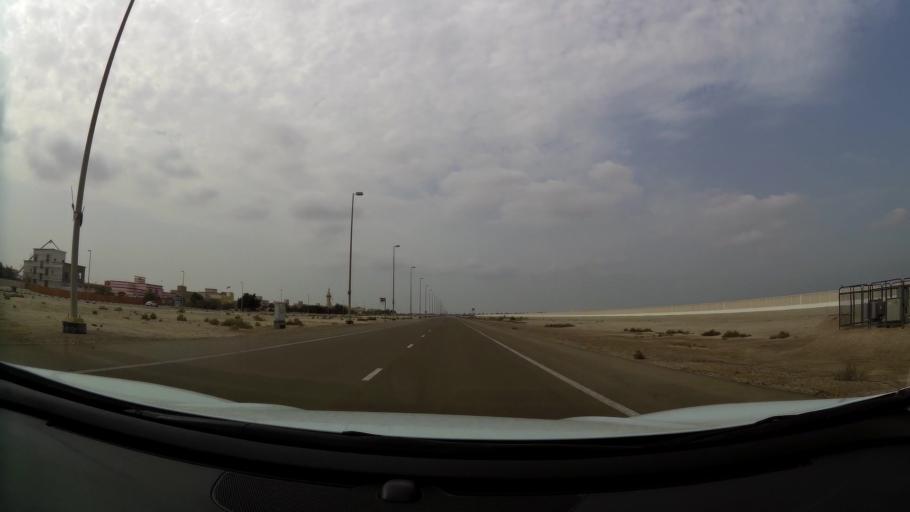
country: AE
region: Abu Dhabi
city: Abu Dhabi
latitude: 24.6371
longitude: 54.6616
